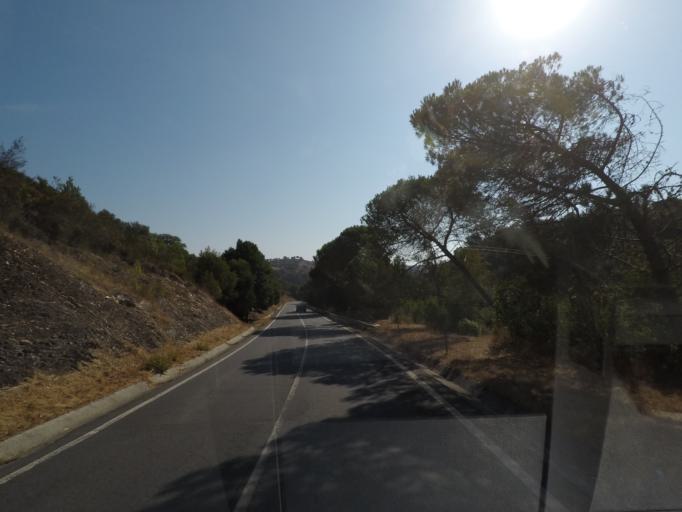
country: PT
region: Beja
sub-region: Odemira
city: Odemira
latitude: 37.6110
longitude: -8.7170
